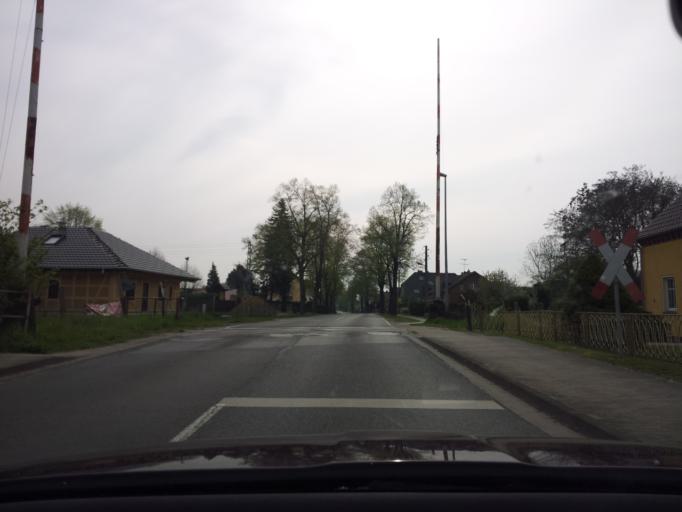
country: DE
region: Brandenburg
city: Drahnsdorf
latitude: 51.8533
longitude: 13.6081
